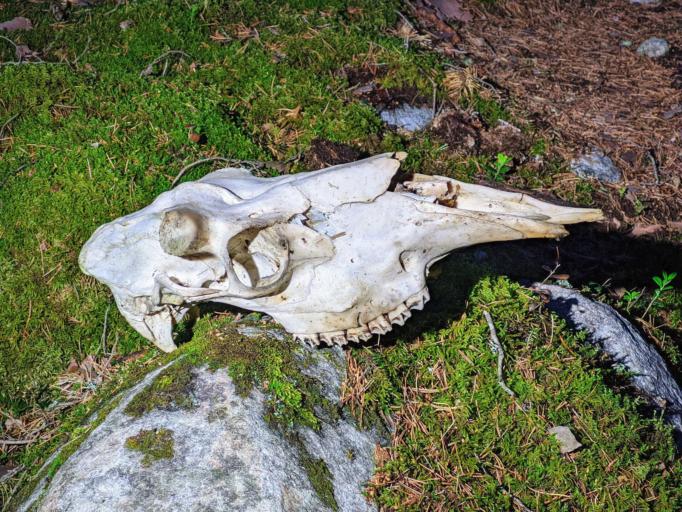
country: NO
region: Buskerud
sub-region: Gol
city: Gol
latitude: 60.7070
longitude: 8.9593
